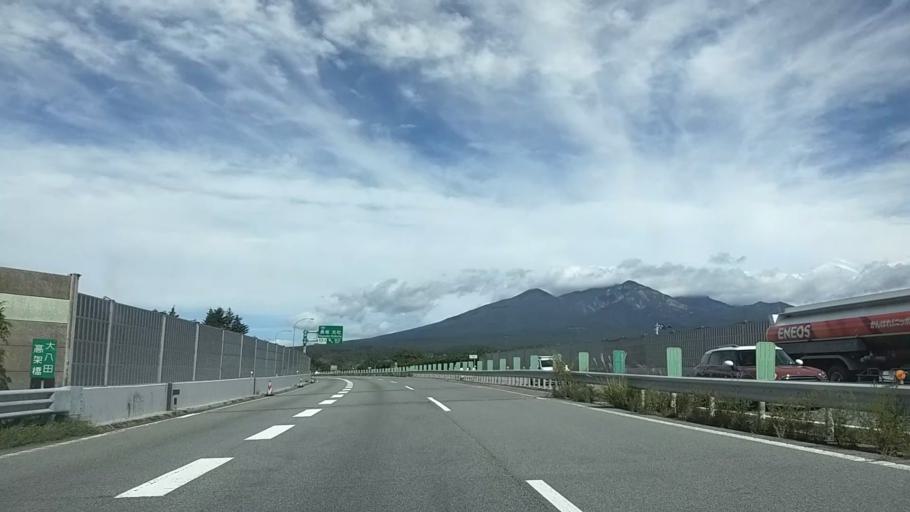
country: JP
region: Yamanashi
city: Nirasaki
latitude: 35.8332
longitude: 138.3917
